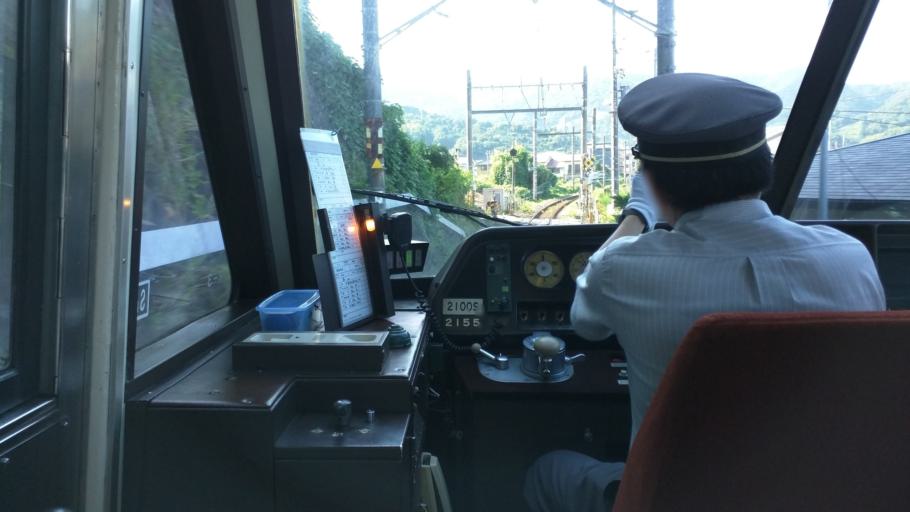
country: JP
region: Shizuoka
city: Ito
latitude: 35.0012
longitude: 139.0808
